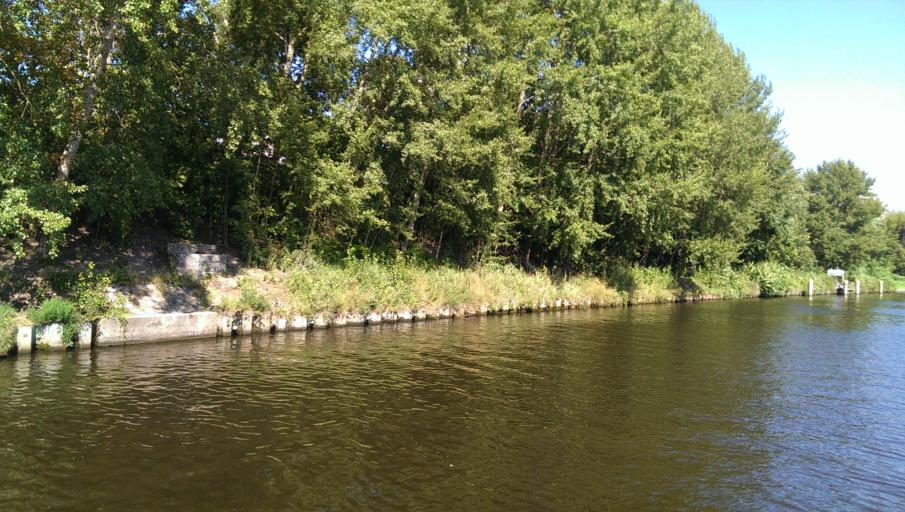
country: DE
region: Berlin
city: Steglitz Bezirk
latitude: 52.4426
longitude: 13.3249
